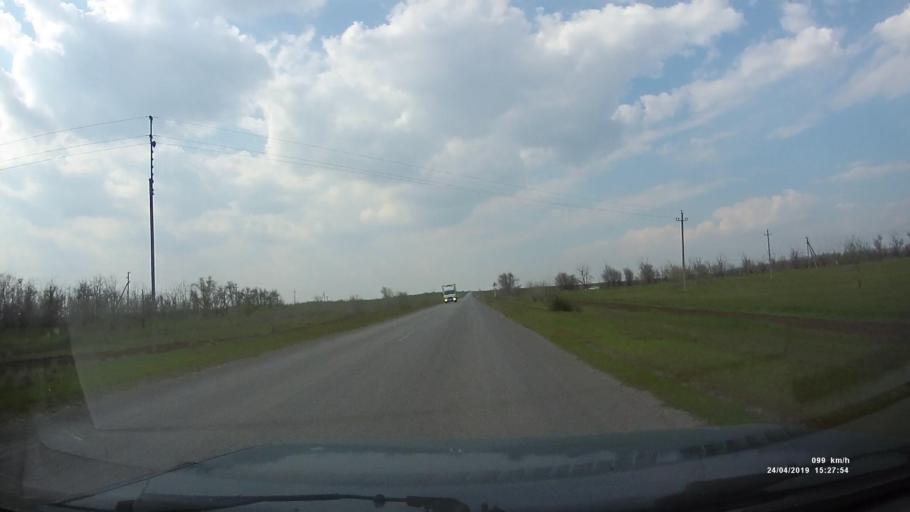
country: RU
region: Rostov
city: Remontnoye
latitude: 46.5713
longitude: 43.0224
